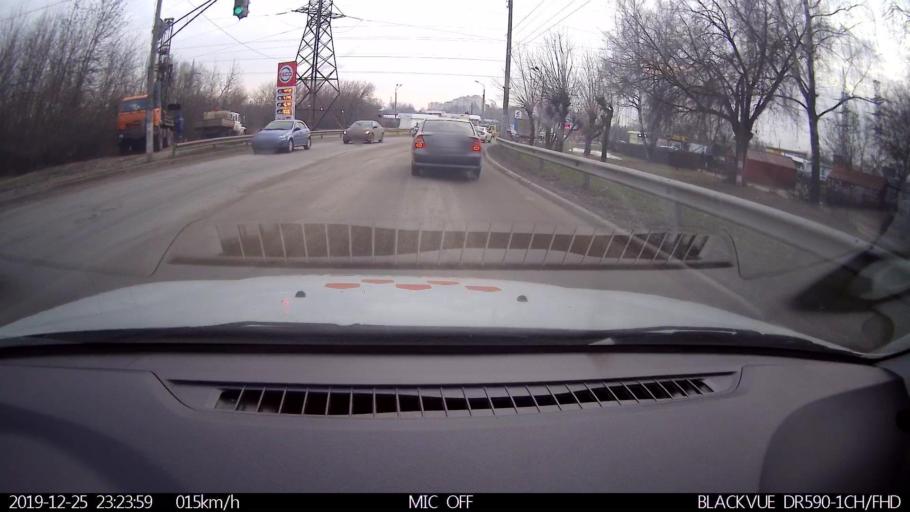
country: RU
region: Nizjnij Novgorod
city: Gorbatovka
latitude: 56.3507
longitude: 43.8366
